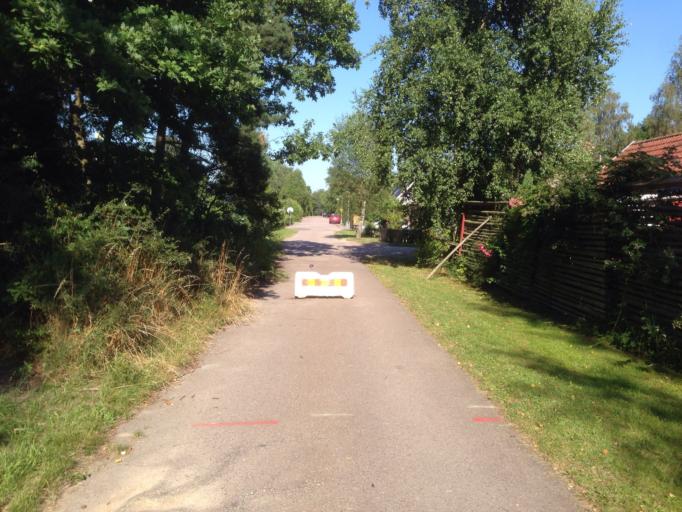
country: SE
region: Kalmar
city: Faerjestaden
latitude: 56.6599
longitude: 16.4802
